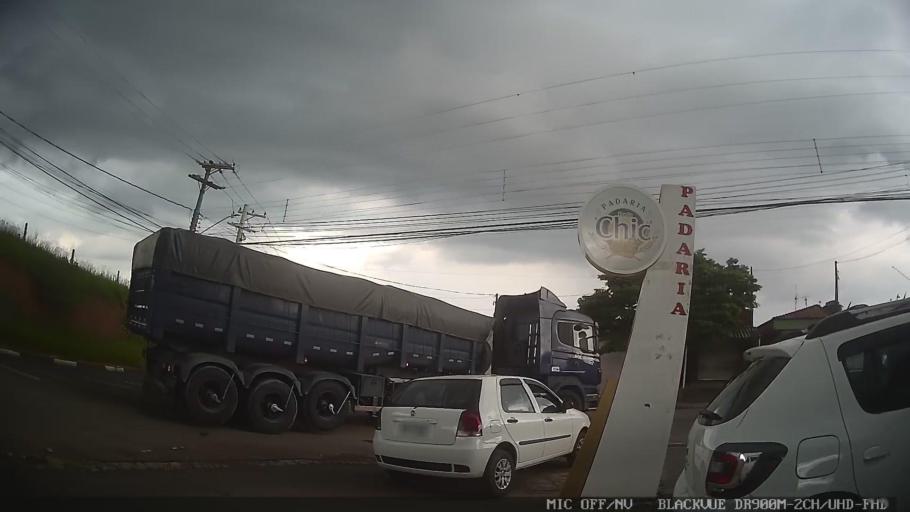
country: BR
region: Sao Paulo
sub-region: Atibaia
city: Atibaia
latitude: -23.1447
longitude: -46.5884
